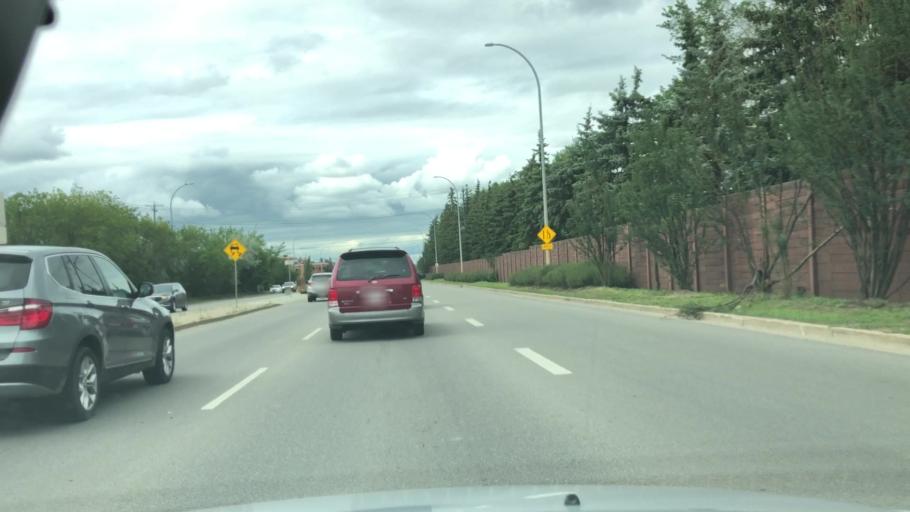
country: CA
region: Alberta
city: Edmonton
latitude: 53.5419
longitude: -113.4433
